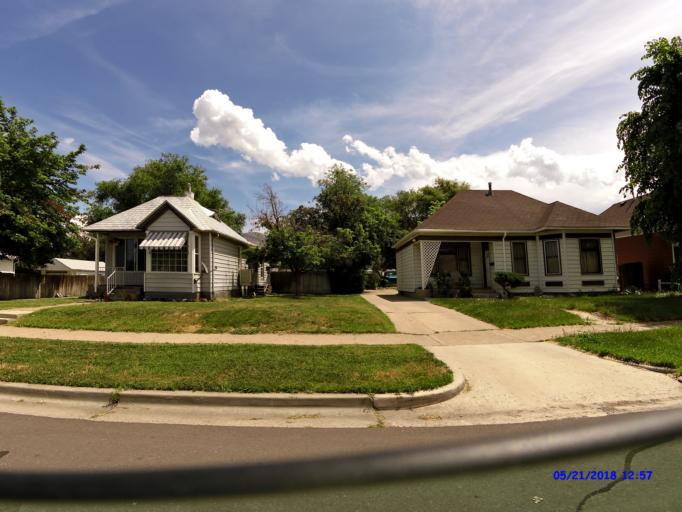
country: US
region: Utah
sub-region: Weber County
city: South Ogden
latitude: 41.2053
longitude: -111.9764
